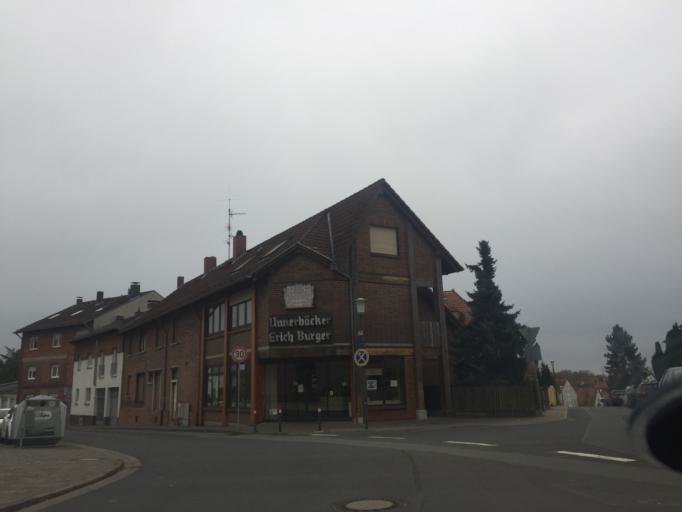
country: DE
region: Hesse
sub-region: Regierungsbezirk Darmstadt
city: Maintal
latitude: 50.1521
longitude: 8.8321
